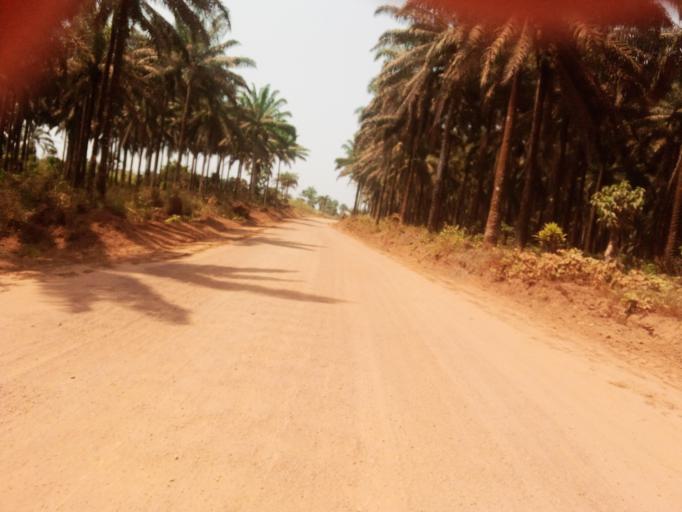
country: SL
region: Southern Province
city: Sumbuya
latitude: 7.6203
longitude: -12.1243
